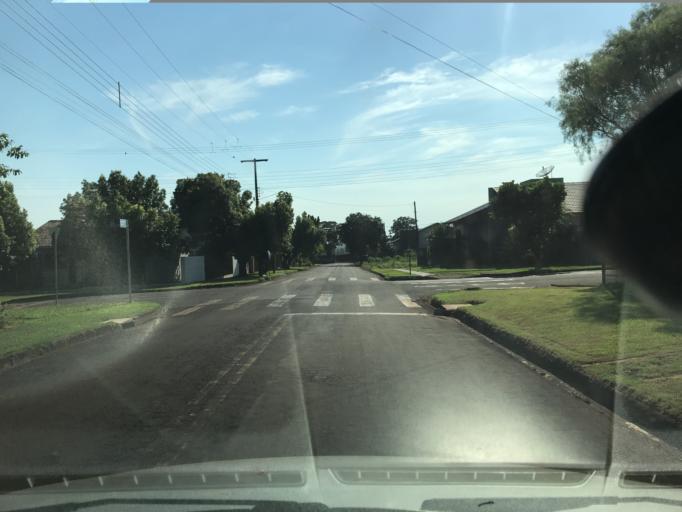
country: BR
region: Parana
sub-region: Palotina
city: Palotina
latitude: -24.2963
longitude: -53.8336
